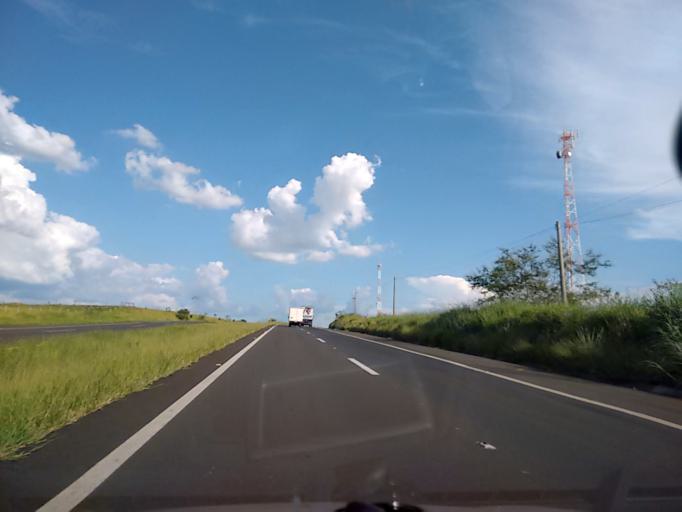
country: BR
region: Sao Paulo
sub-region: Duartina
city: Duartina
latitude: -22.2830
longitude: -49.4935
